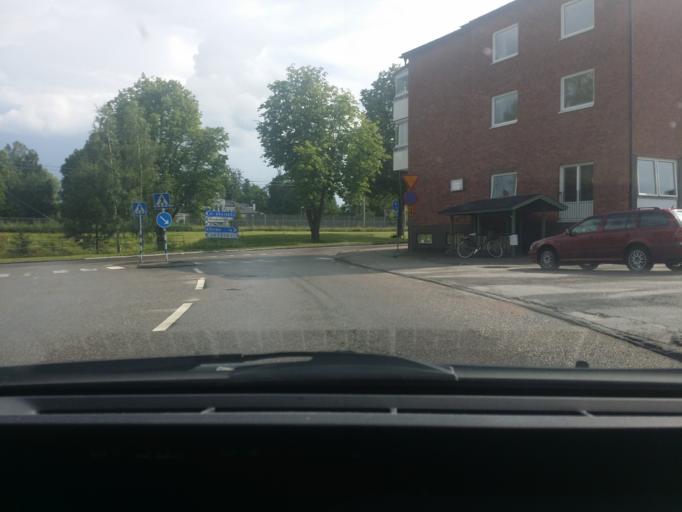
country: SE
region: Vaestmanland
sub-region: Hallstahammars Kommun
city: Kolback
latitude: 59.5657
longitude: 16.2352
